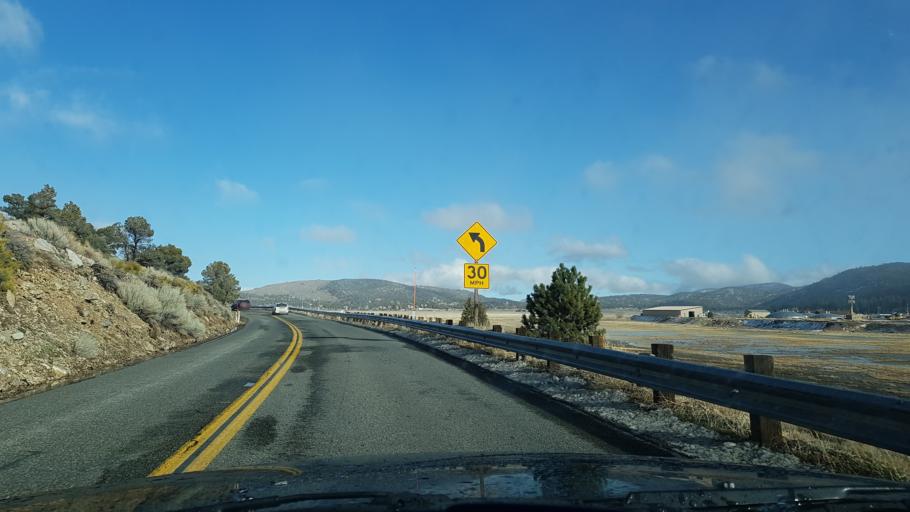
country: US
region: California
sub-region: San Bernardino County
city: Big Bear City
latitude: 34.2725
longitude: -116.8221
